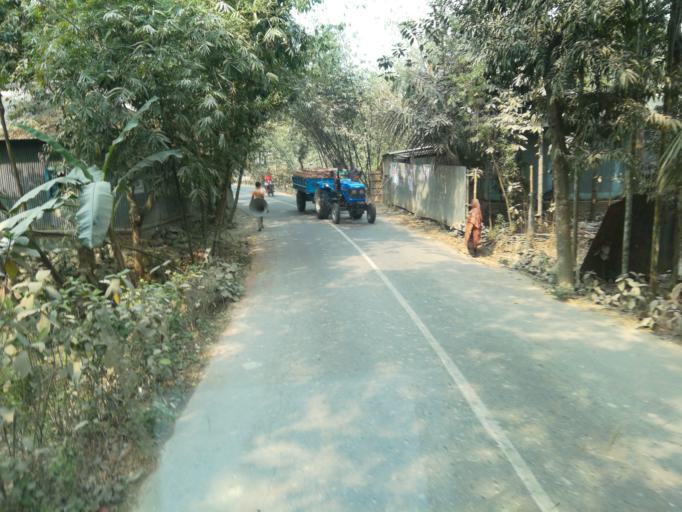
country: BD
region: Dhaka
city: Nagarpur
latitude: 23.9941
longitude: 89.8466
